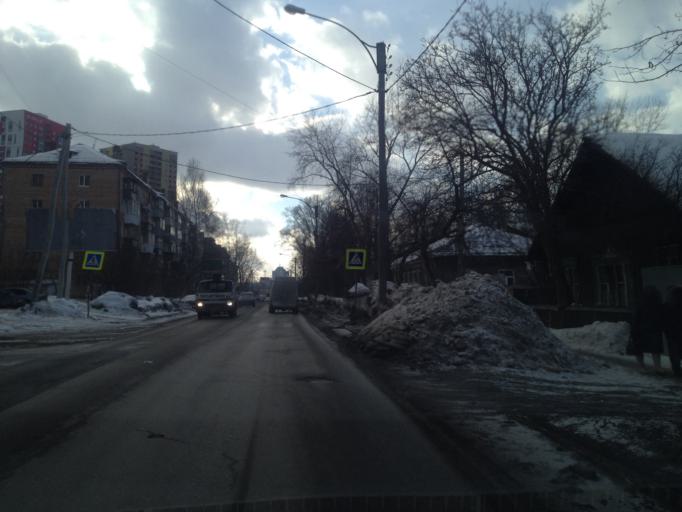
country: RU
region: Sverdlovsk
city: Yekaterinburg
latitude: 56.8630
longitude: 60.6198
